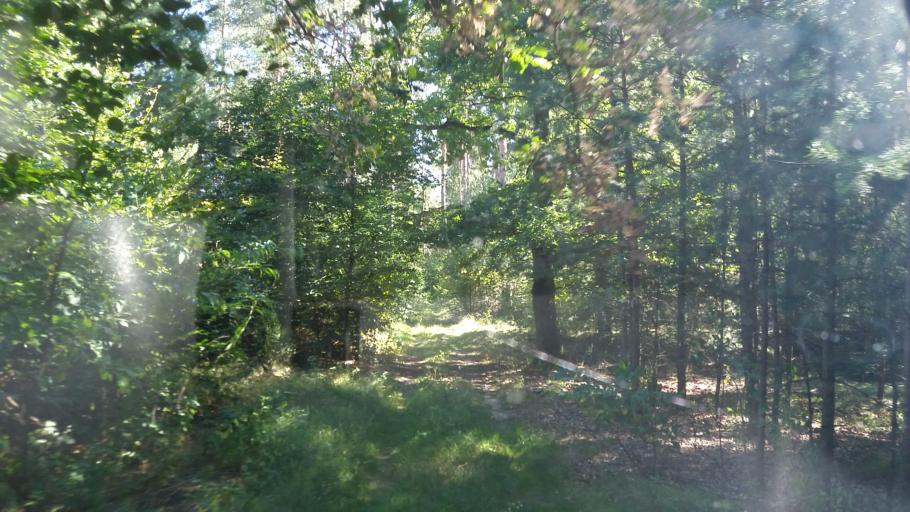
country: PL
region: West Pomeranian Voivodeship
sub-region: Powiat choszczenski
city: Krzecin
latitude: 53.0885
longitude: 15.4477
